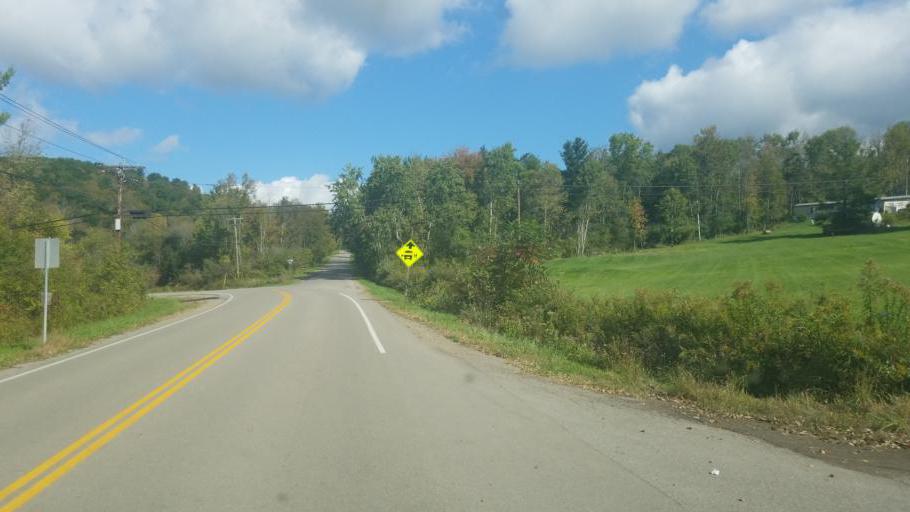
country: US
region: New York
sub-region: Allegany County
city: Cuba
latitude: 42.2525
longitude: -78.2770
